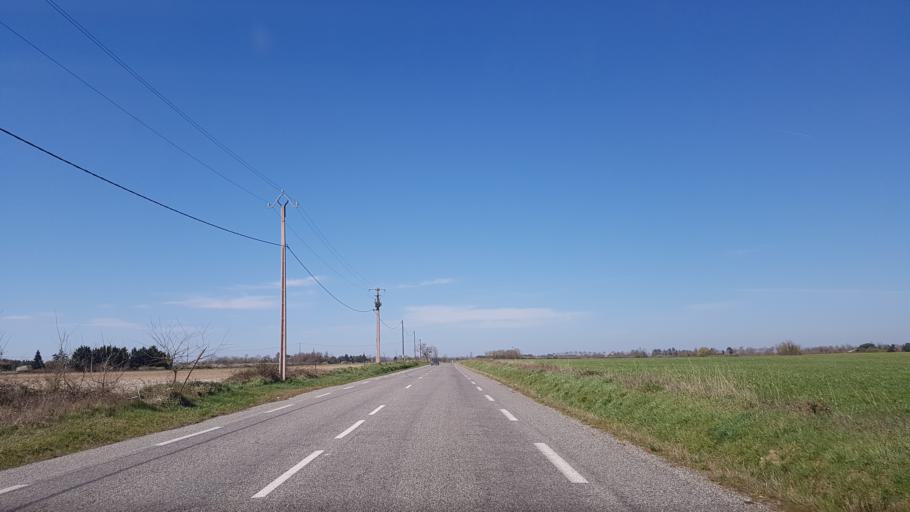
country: FR
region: Midi-Pyrenees
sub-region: Departement de l'Ariege
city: Mazeres
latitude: 43.2286
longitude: 1.6745
